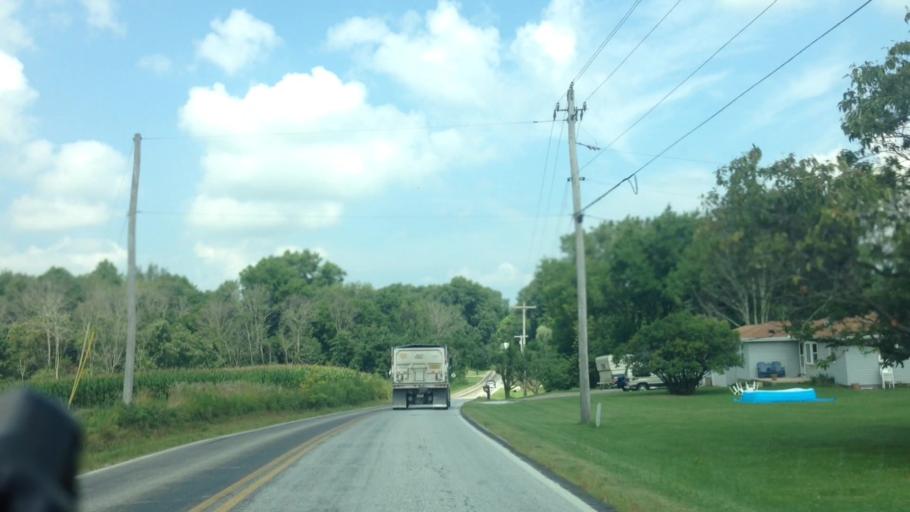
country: US
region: Ohio
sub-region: Wayne County
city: Dalton
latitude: 40.8591
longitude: -81.6637
